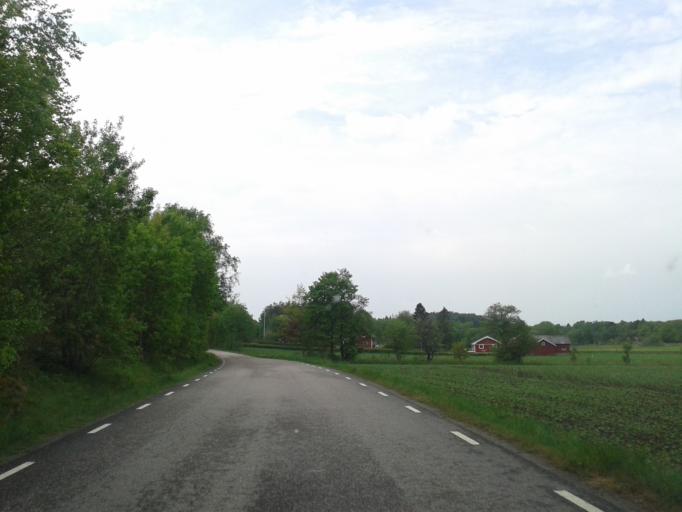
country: SE
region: Vaestra Goetaland
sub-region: Kungalvs Kommun
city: Kungalv
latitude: 57.9177
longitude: 11.9259
